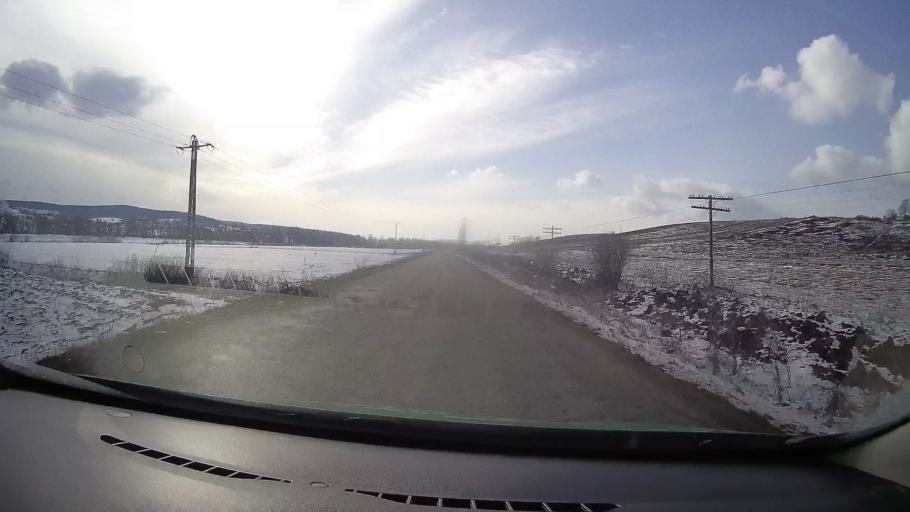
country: RO
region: Sibiu
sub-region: Comuna Iacobeni
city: Iacobeni
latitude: 46.0456
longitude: 24.7609
